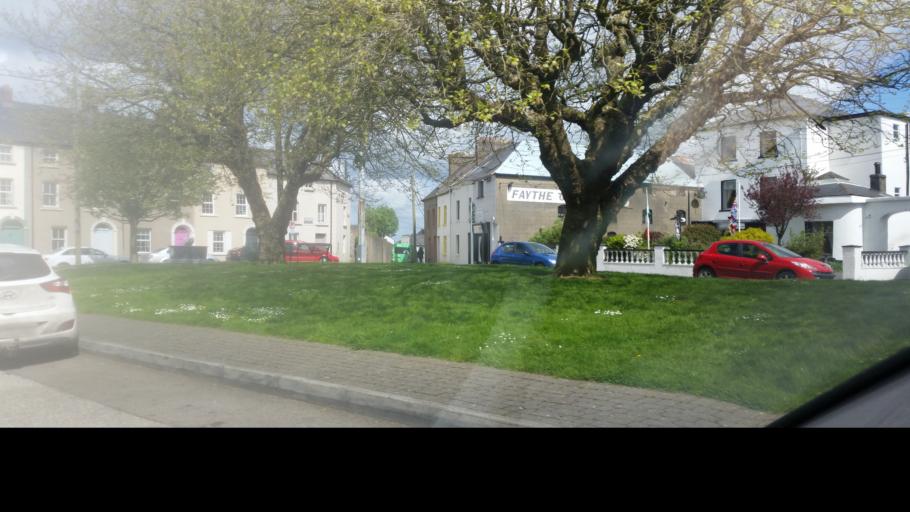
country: IE
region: Leinster
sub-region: Loch Garman
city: Loch Garman
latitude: 52.3326
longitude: -6.4576
